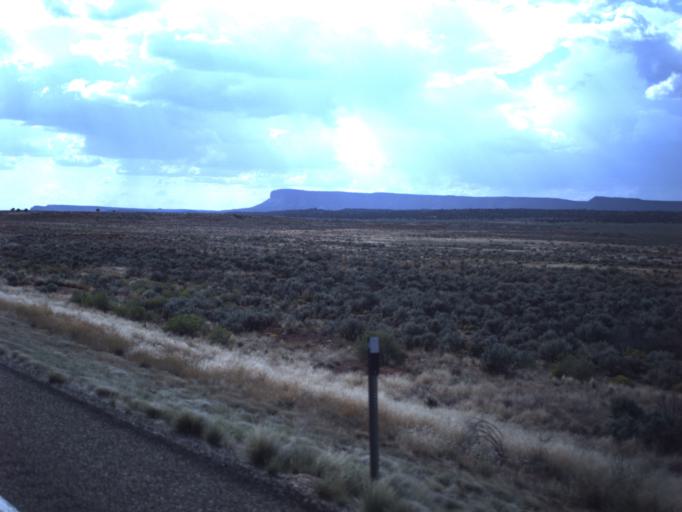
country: US
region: Utah
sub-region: Kane County
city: Kanab
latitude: 37.1232
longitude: -112.0998
